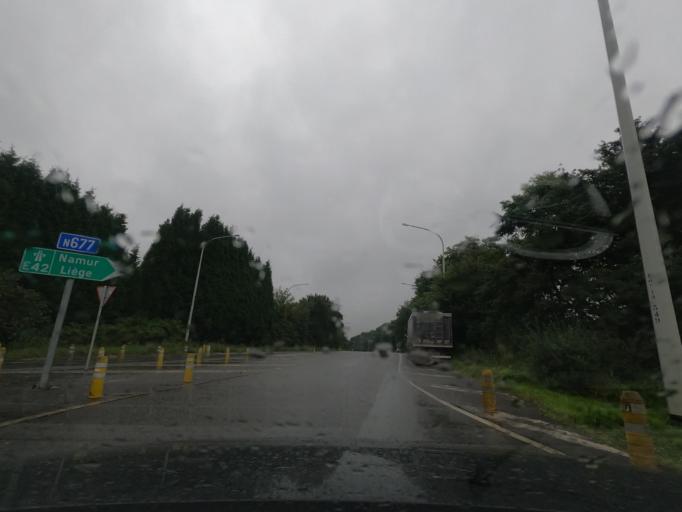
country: BE
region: Wallonia
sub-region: Province de Liege
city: Flemalle-Haute
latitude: 50.6139
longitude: 5.4416
